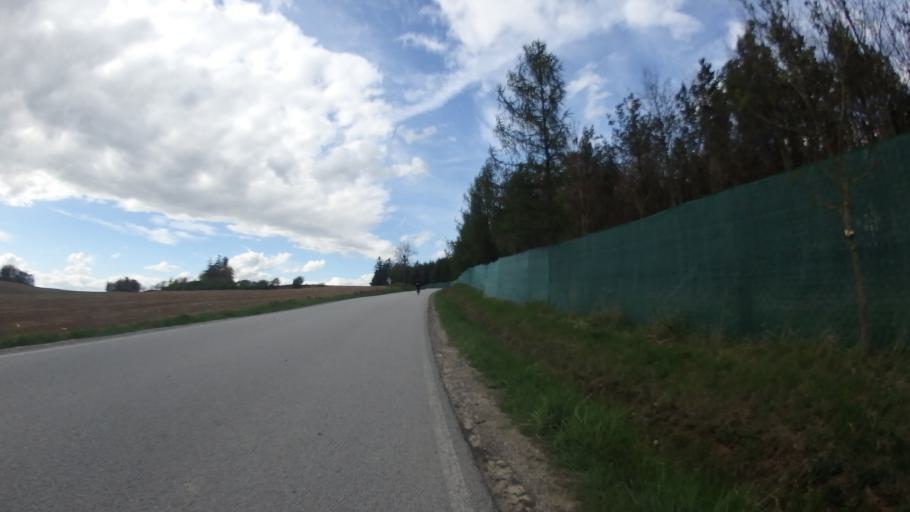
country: CZ
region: Vysocina
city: Merin
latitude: 49.3649
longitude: 15.9011
